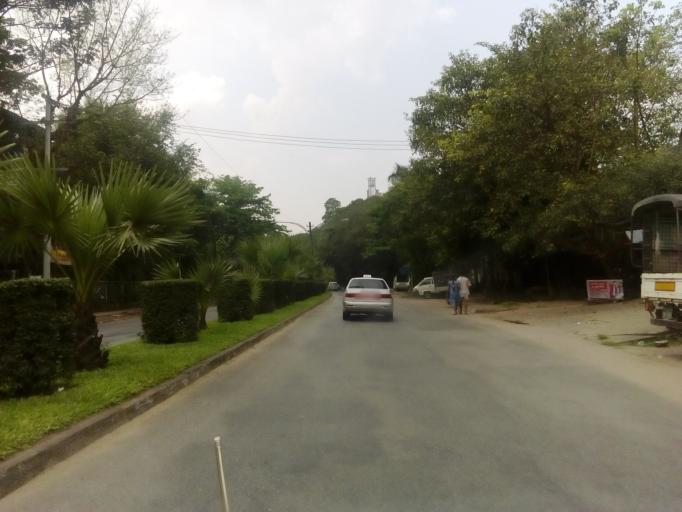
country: MM
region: Yangon
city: Yangon
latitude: 16.7891
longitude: 96.1604
